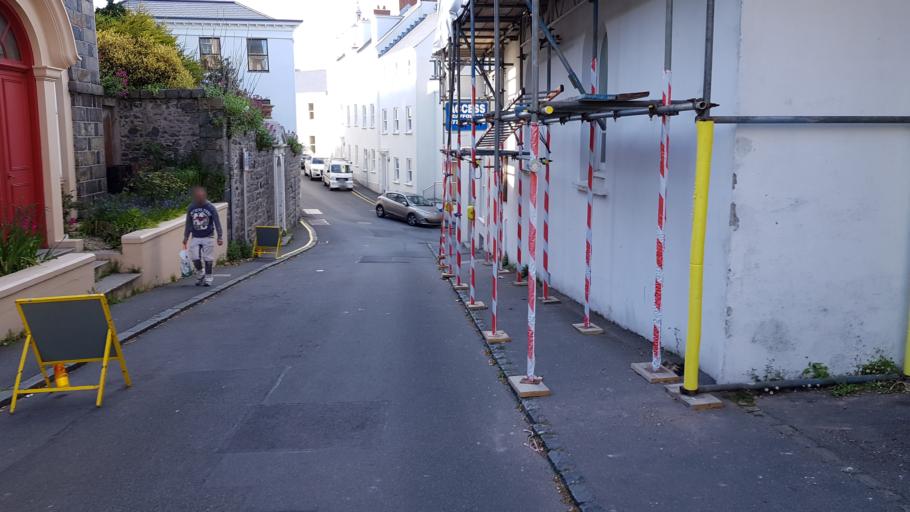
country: GG
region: St Peter Port
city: Saint Peter Port
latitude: 49.4554
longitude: -2.5387
